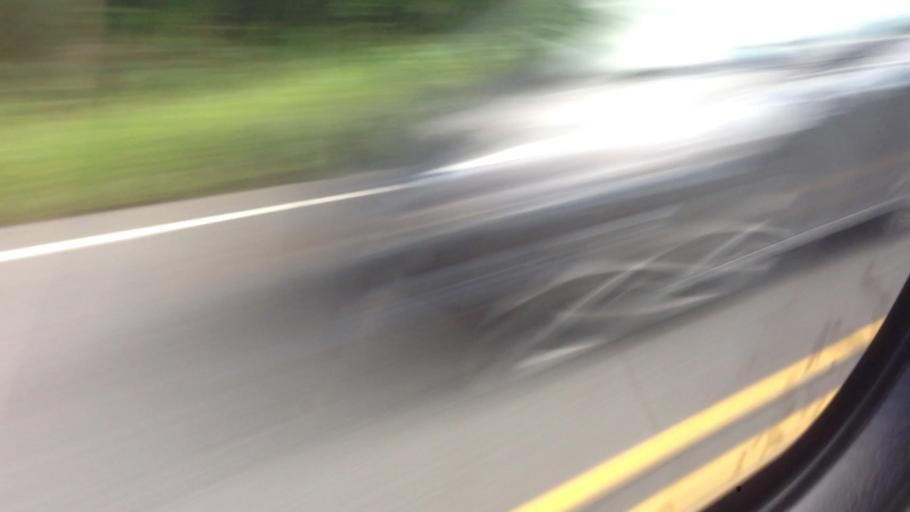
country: US
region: New York
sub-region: Dutchess County
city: Tivoli
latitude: 42.0436
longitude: -73.8954
